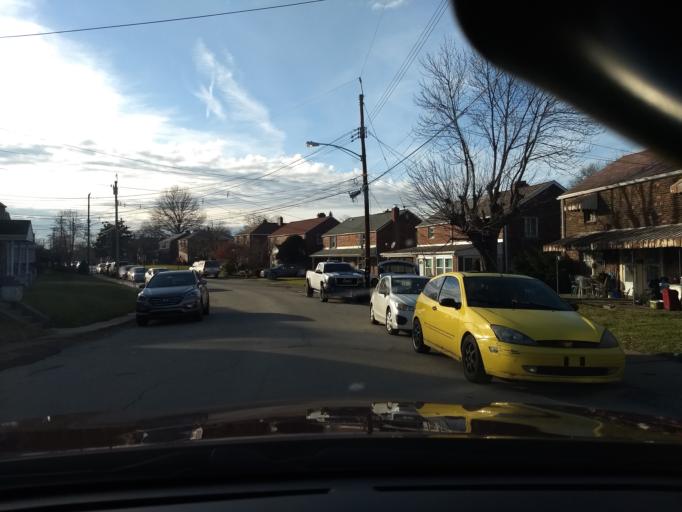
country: US
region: Pennsylvania
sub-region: Allegheny County
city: Whitaker
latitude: 40.4040
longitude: -79.8876
